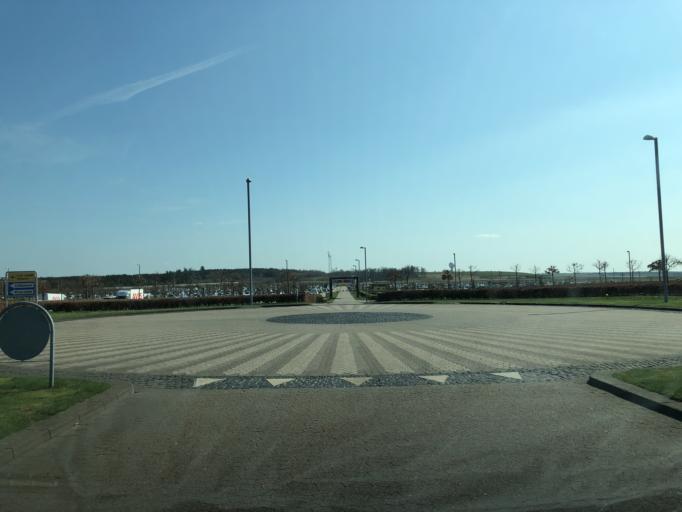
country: DK
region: South Denmark
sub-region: Billund Kommune
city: Billund
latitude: 55.7468
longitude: 9.1498
